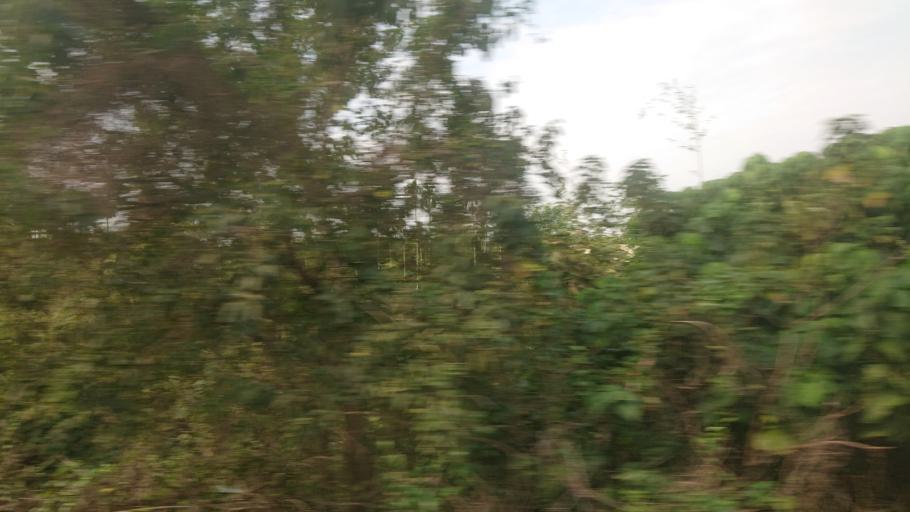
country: TW
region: Taiwan
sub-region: Nantou
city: Nantou
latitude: 23.8882
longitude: 120.5823
